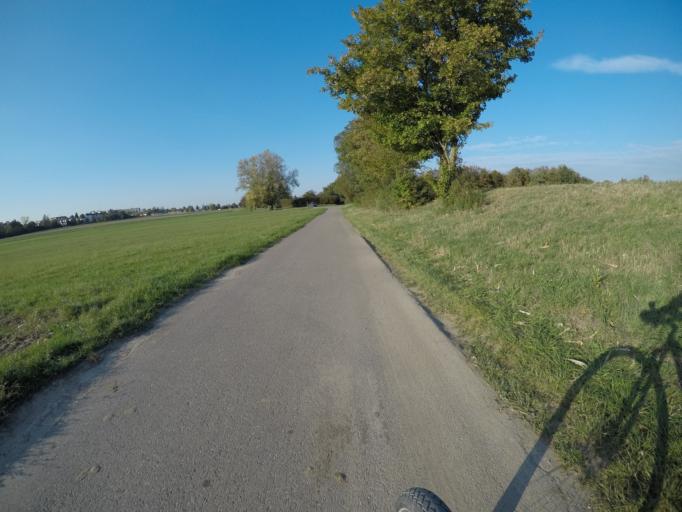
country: DE
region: Baden-Wuerttemberg
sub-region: Regierungsbezirk Stuttgart
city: Ostfildern
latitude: 48.7339
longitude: 9.2365
